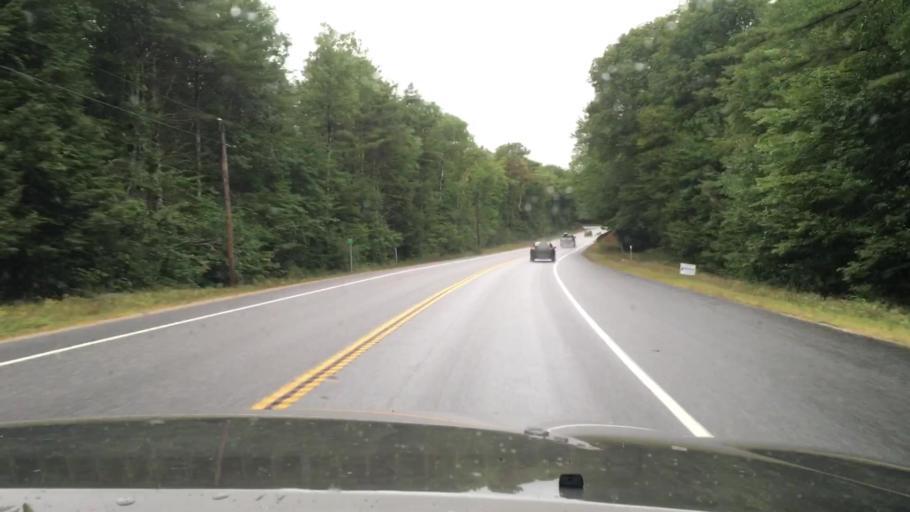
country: US
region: New Hampshire
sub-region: Hillsborough County
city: Antrim
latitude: 43.0706
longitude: -72.0354
